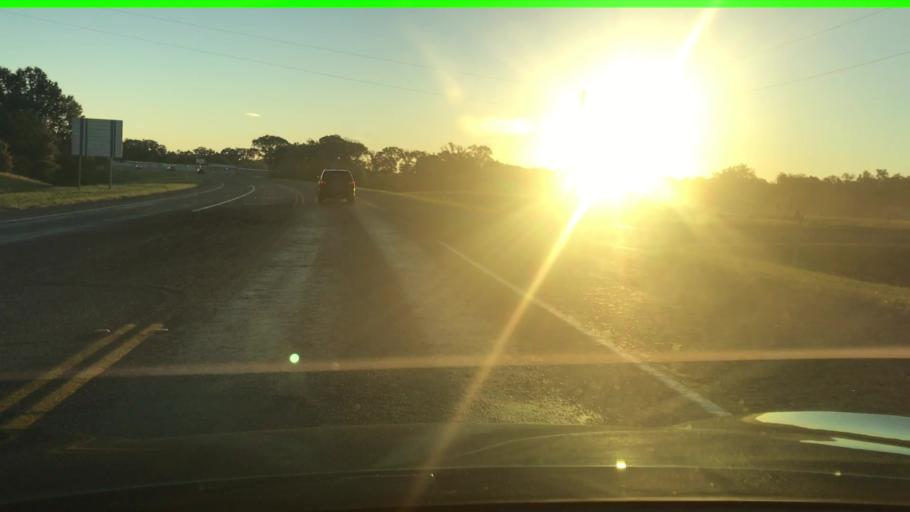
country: US
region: Texas
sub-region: Henderson County
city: Athens
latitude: 32.1714
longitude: -95.8305
